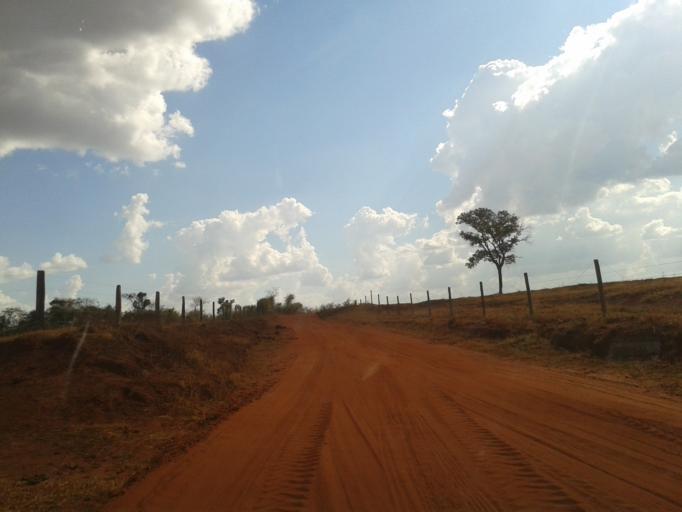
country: BR
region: Minas Gerais
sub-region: Santa Vitoria
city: Santa Vitoria
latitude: -19.2744
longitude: -49.9977
